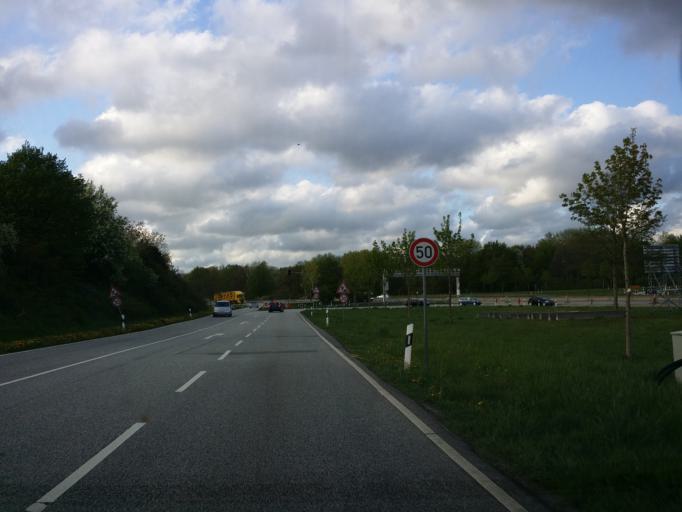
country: DE
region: Schleswig-Holstein
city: Westerronfeld
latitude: 54.2952
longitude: 9.6530
